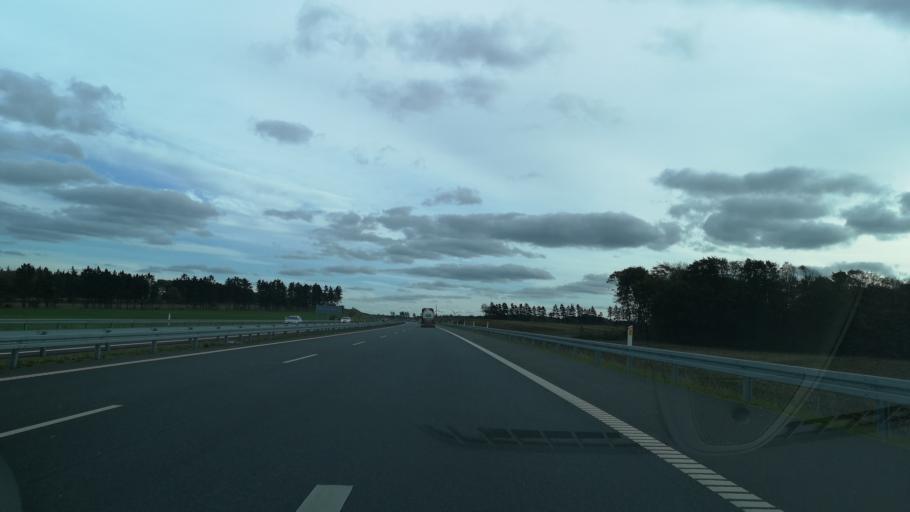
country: DK
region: Central Jutland
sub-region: Herning Kommune
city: Avlum
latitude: 56.2888
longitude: 8.7312
